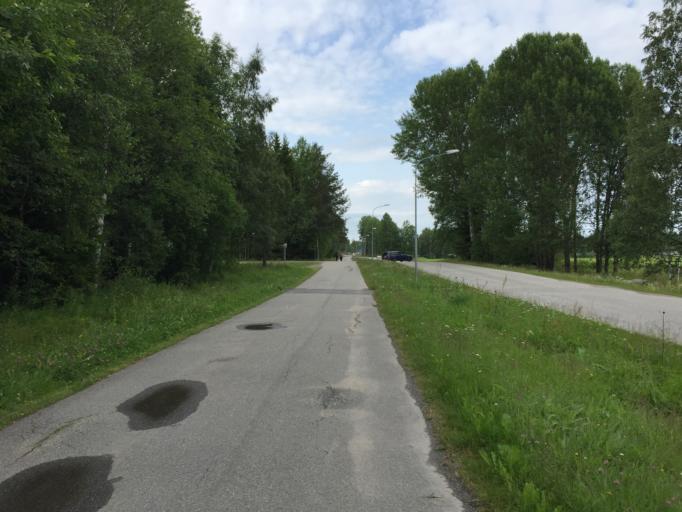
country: SE
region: Vaesterbotten
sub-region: Umea Kommun
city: Ersmark
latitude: 63.8392
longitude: 20.3389
